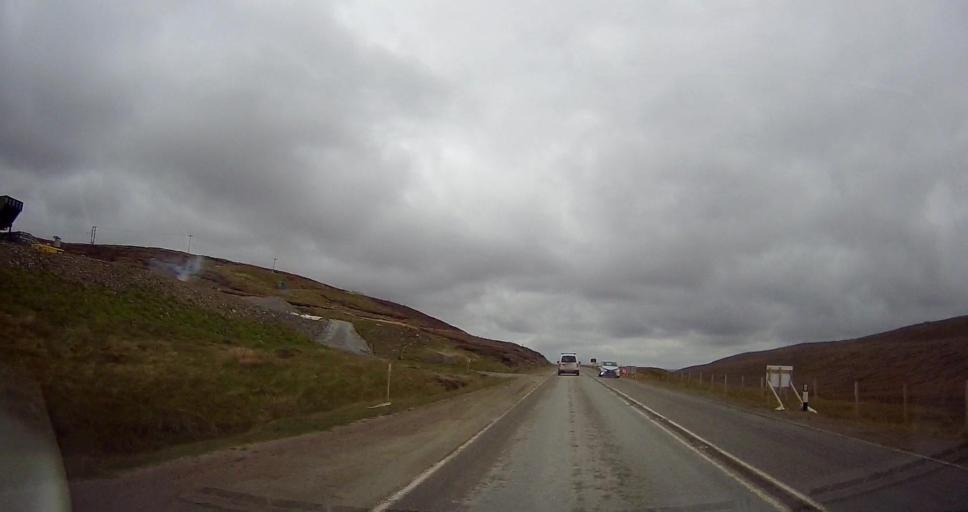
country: GB
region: Scotland
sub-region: Shetland Islands
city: Lerwick
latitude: 60.3257
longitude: -1.2527
